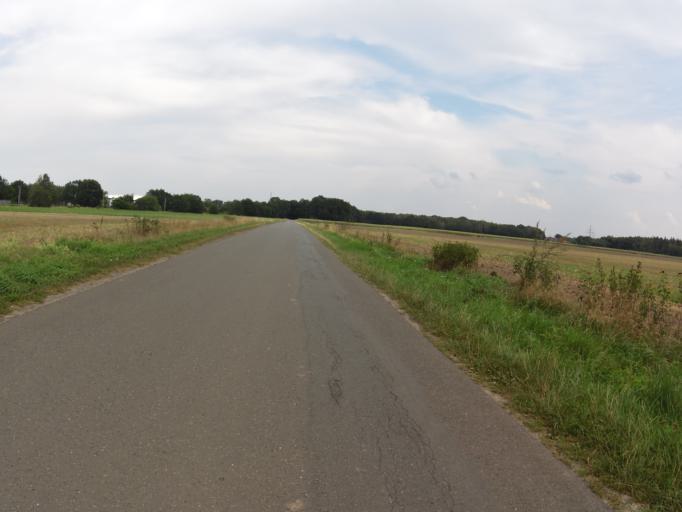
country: DE
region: Lower Saxony
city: Estorf
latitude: 52.6052
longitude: 9.1887
